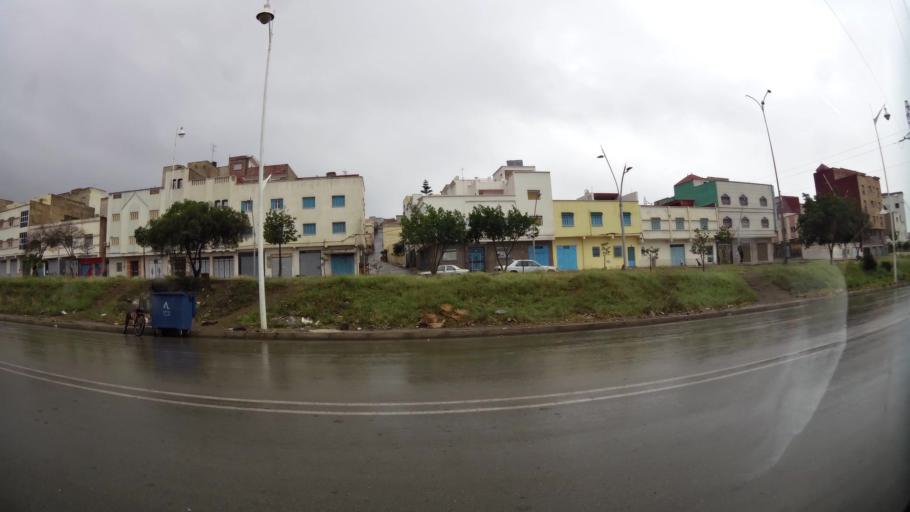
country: MA
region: Oriental
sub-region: Nador
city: Nador
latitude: 35.1551
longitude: -2.9766
